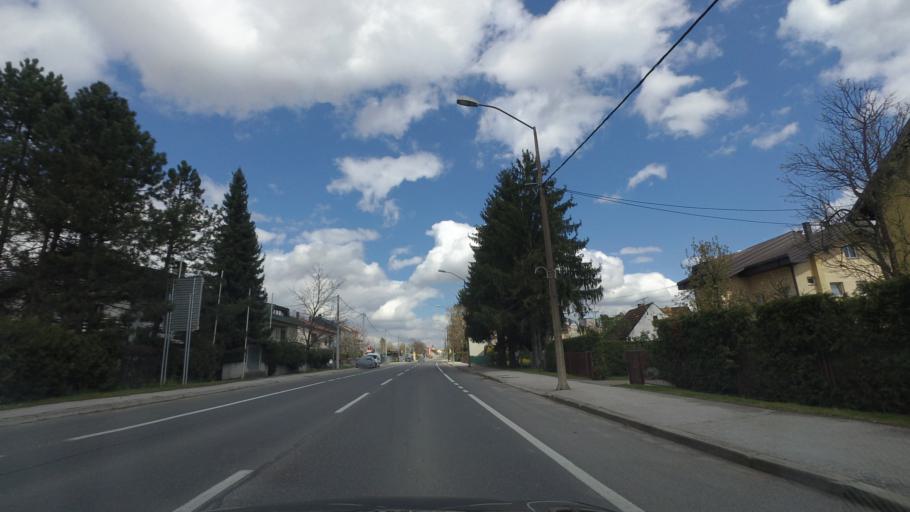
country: HR
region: Zagrebacka
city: Jastrebarsko
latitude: 45.6614
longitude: 15.6414
